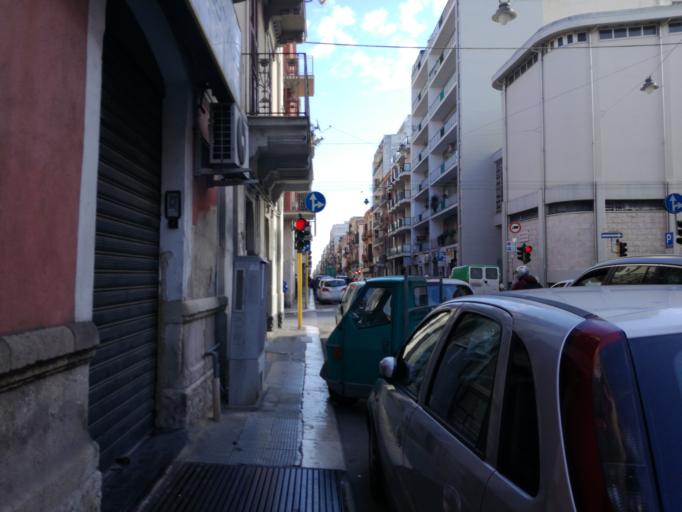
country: IT
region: Apulia
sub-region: Provincia di Bari
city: Bari
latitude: 41.1214
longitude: 16.8584
